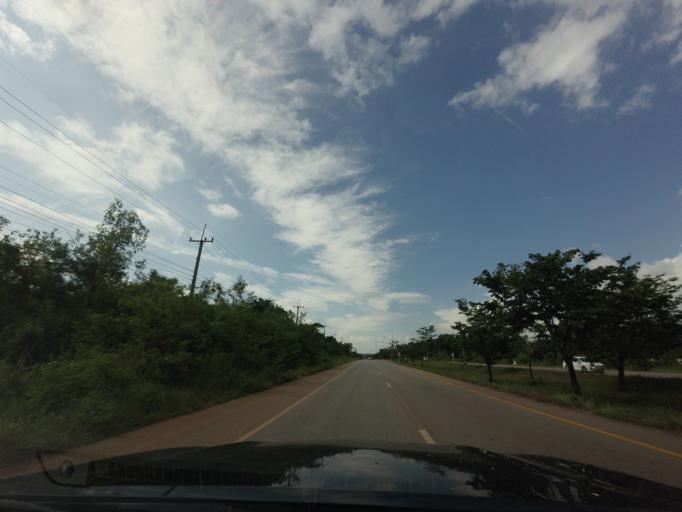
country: TH
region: Nong Khai
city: Sa Khrai
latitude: 17.6019
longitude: 102.7947
